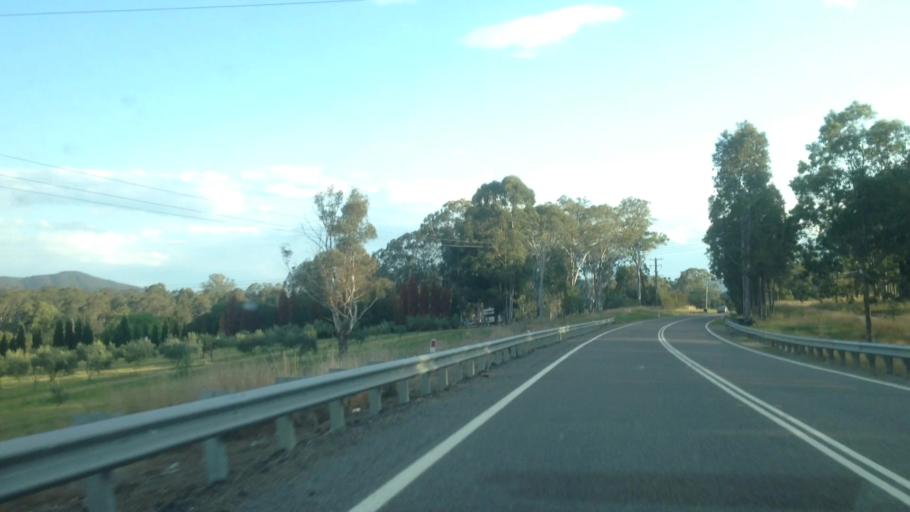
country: AU
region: New South Wales
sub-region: Cessnock
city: Kurri Kurri
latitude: -32.8690
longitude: 151.4795
